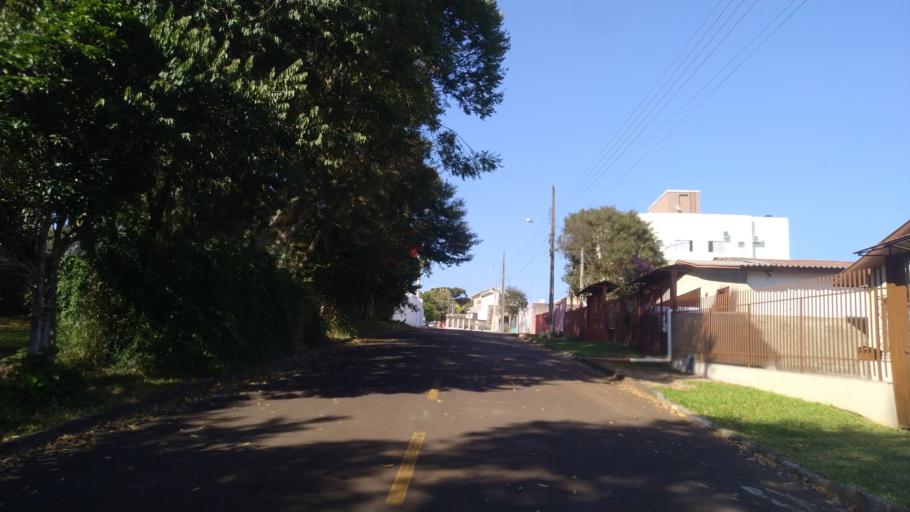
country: BR
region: Santa Catarina
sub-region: Chapeco
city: Chapeco
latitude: -27.0780
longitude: -52.6028
